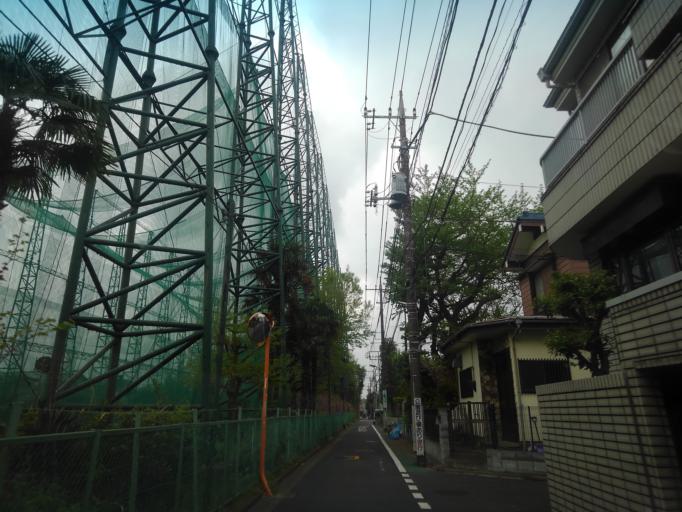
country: JP
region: Tokyo
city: Musashino
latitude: 35.7208
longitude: 139.5869
